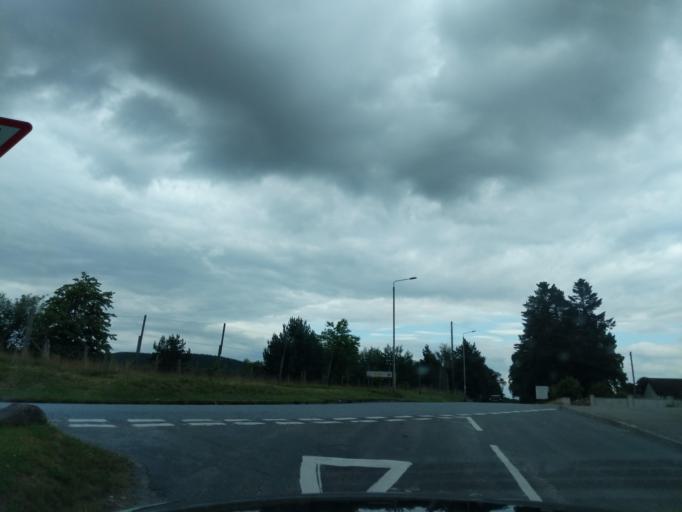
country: GB
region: Scotland
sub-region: Highland
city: Aviemore
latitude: 57.2845
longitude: -3.8152
